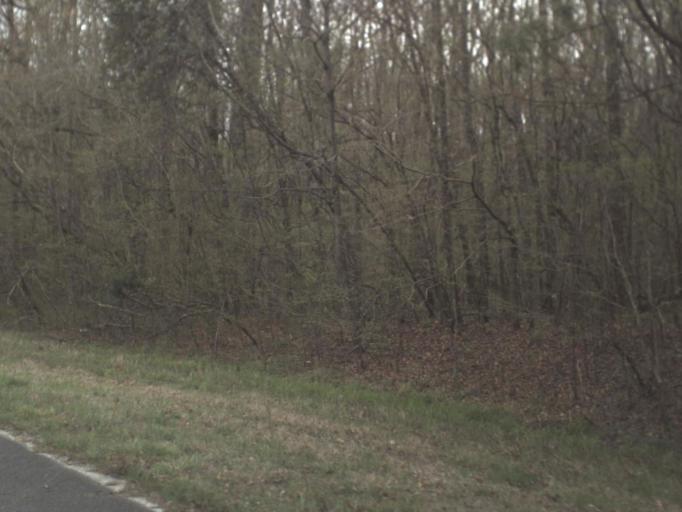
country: US
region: Florida
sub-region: Wakulla County
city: Crawfordville
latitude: 30.2468
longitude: -84.3172
